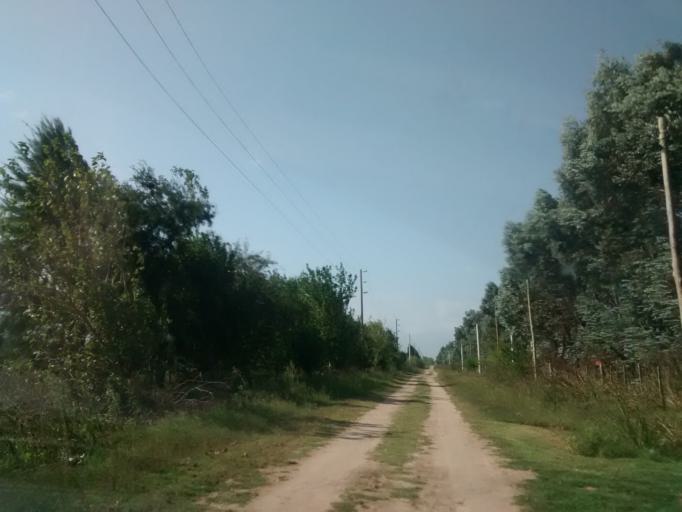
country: AR
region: Buenos Aires
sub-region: Partido de La Plata
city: La Plata
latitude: -35.0098
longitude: -57.9068
